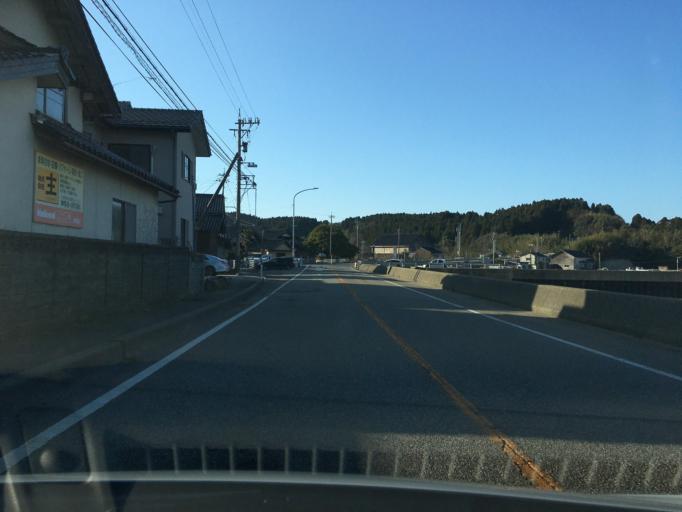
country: JP
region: Ishikawa
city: Nanao
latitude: 36.9762
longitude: 137.0502
